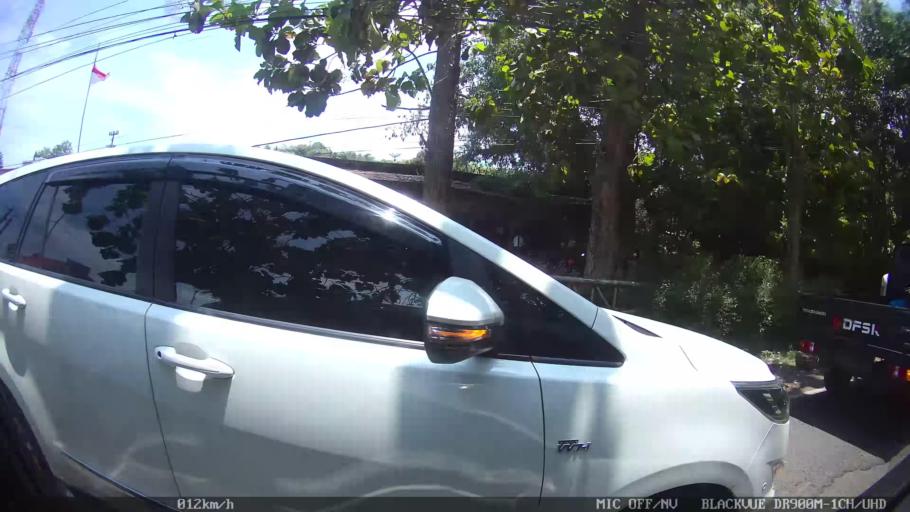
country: ID
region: Lampung
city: Kedaton
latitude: -5.4007
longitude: 105.2540
